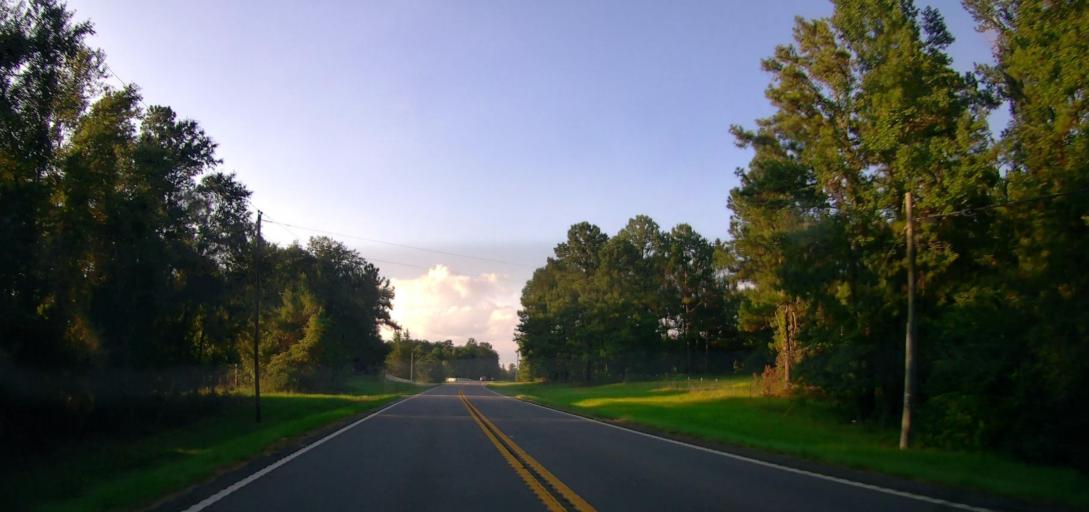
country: US
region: Georgia
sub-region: Taylor County
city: Reynolds
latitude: 32.6187
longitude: -84.1004
